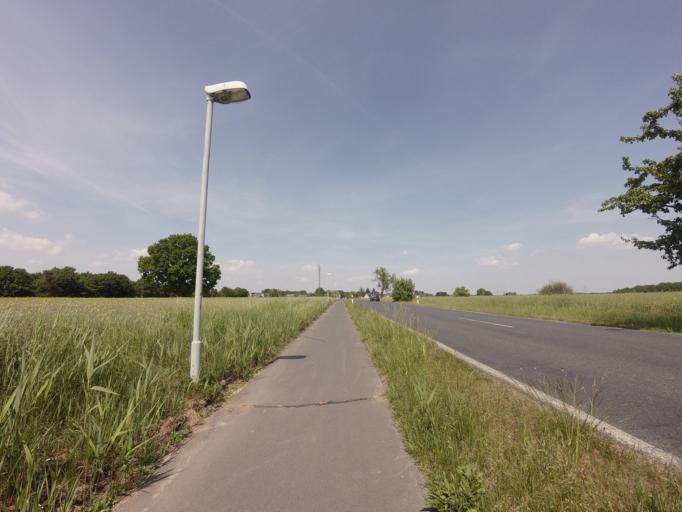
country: DE
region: Lower Saxony
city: Cremlingen
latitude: 52.2848
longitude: 10.6033
